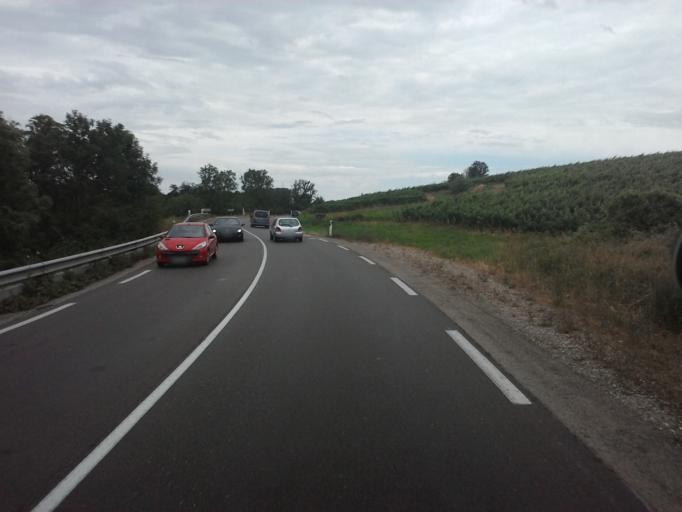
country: FR
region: Franche-Comte
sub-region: Departement du Jura
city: Poligny
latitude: 46.8788
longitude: 5.7178
